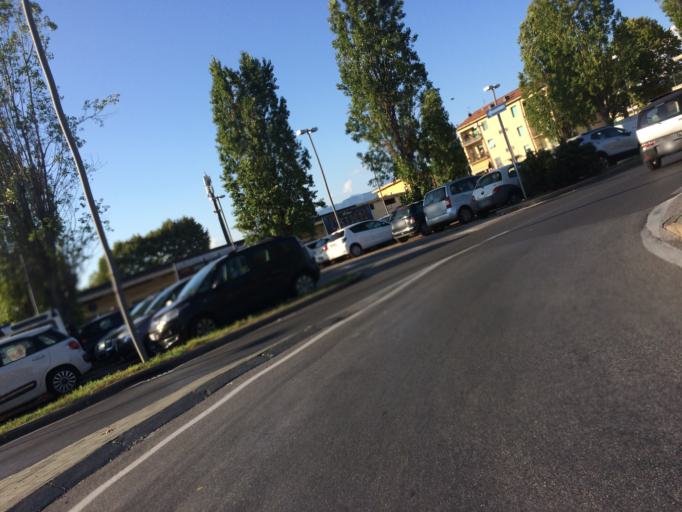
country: IT
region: Tuscany
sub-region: Provincia di Lucca
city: Viareggio
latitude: 43.8652
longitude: 10.2570
